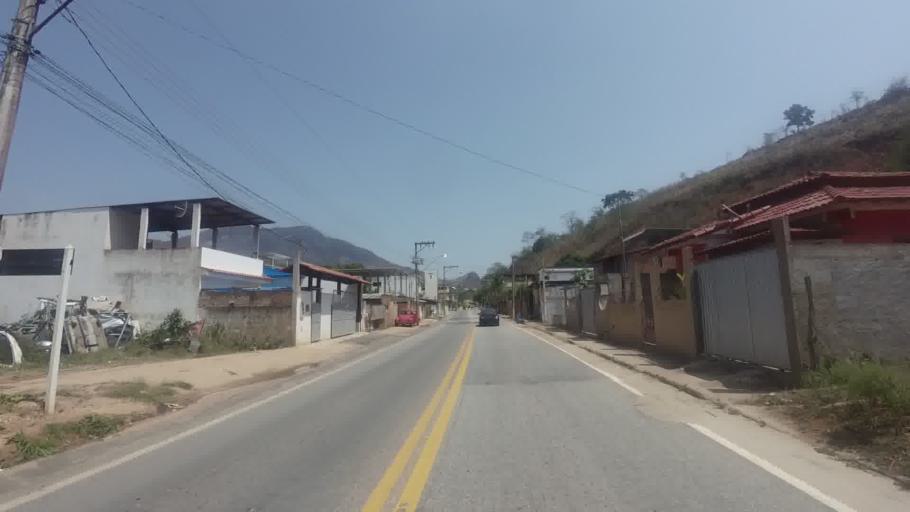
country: BR
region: Espirito Santo
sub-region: Mimoso Do Sul
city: Mimoso do Sul
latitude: -20.9411
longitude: -41.3315
